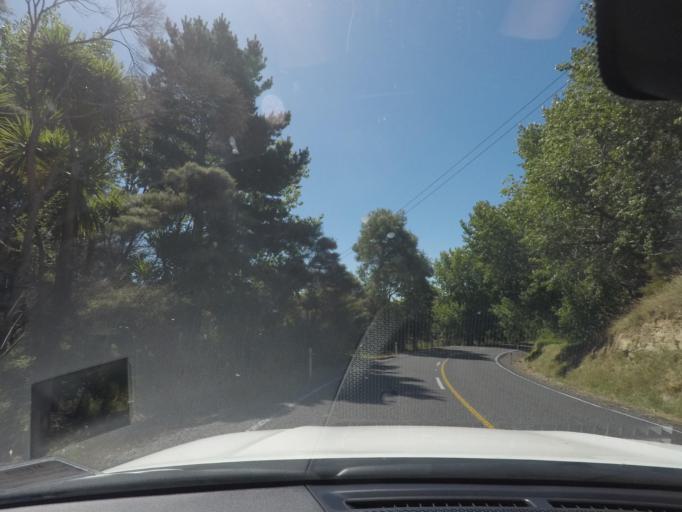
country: NZ
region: Auckland
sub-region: Auckland
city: Parakai
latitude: -36.5924
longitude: 174.3377
